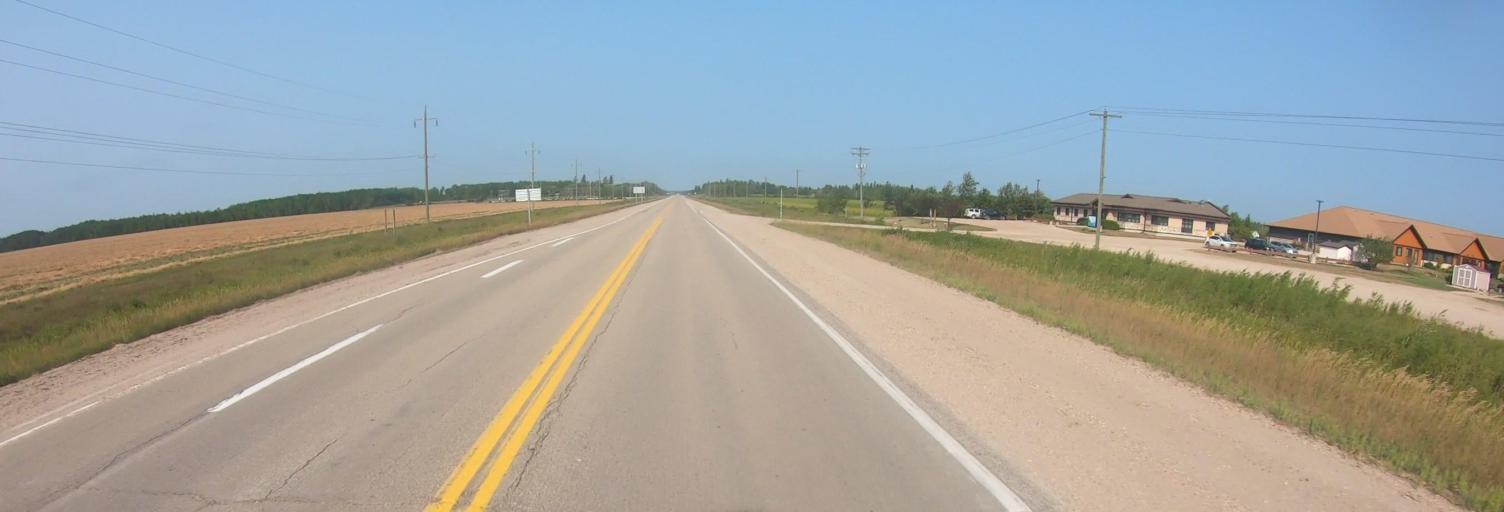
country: US
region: Minnesota
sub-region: Roseau County
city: Roseau
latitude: 49.0233
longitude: -95.6443
